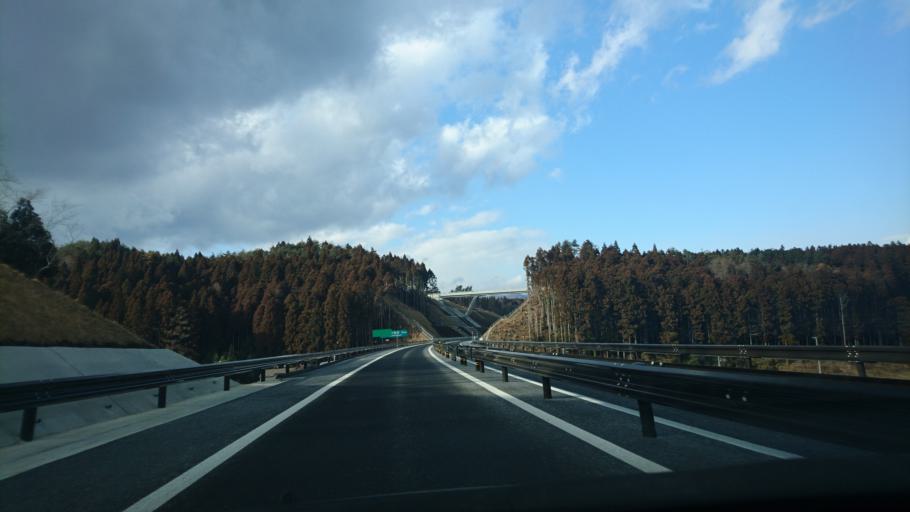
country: JP
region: Miyagi
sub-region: Oshika Gun
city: Onagawa Cho
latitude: 38.7639
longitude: 141.4973
